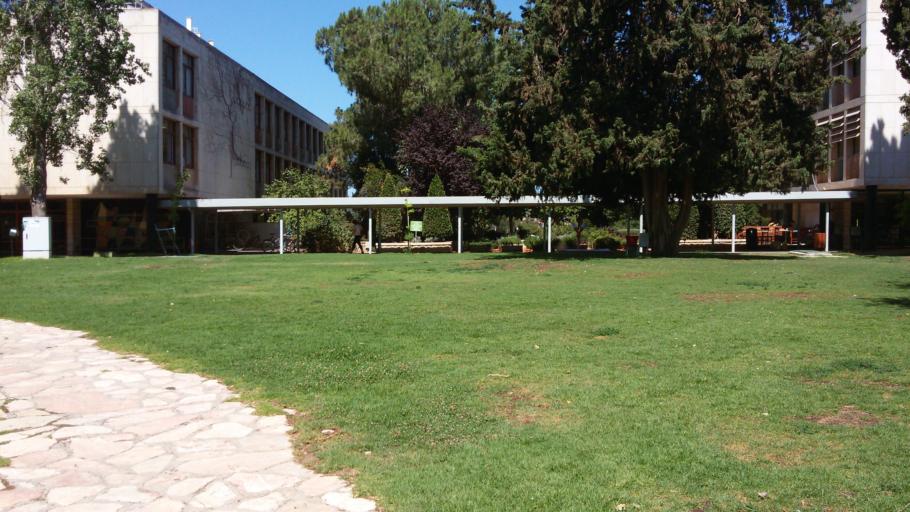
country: IL
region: Jerusalem
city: Jerusalem
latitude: 31.7779
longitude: 35.1965
